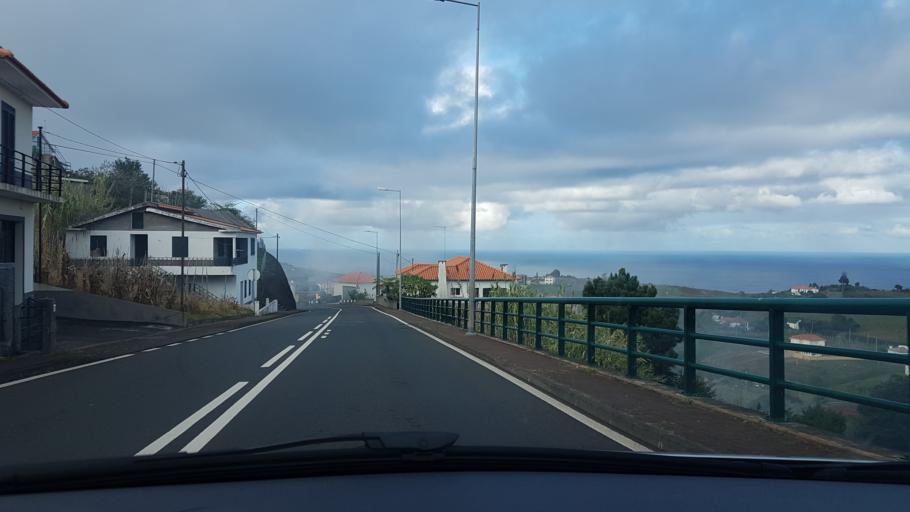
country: PT
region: Madeira
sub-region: Santana
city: Santana
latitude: 32.8203
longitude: -16.8879
